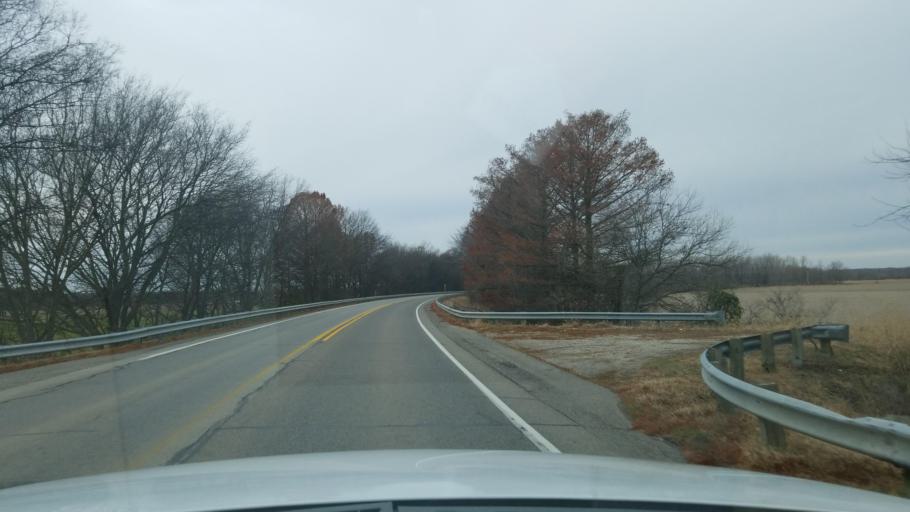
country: US
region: Indiana
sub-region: Posey County
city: Mount Vernon
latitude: 37.9299
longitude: -88.0004
